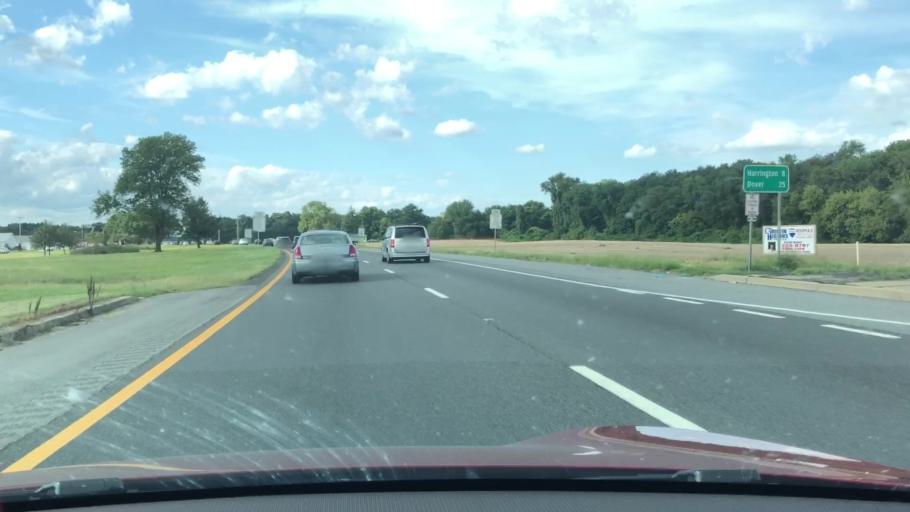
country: US
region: Delaware
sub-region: Sussex County
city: Bridgeville
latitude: 38.8071
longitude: -75.5837
